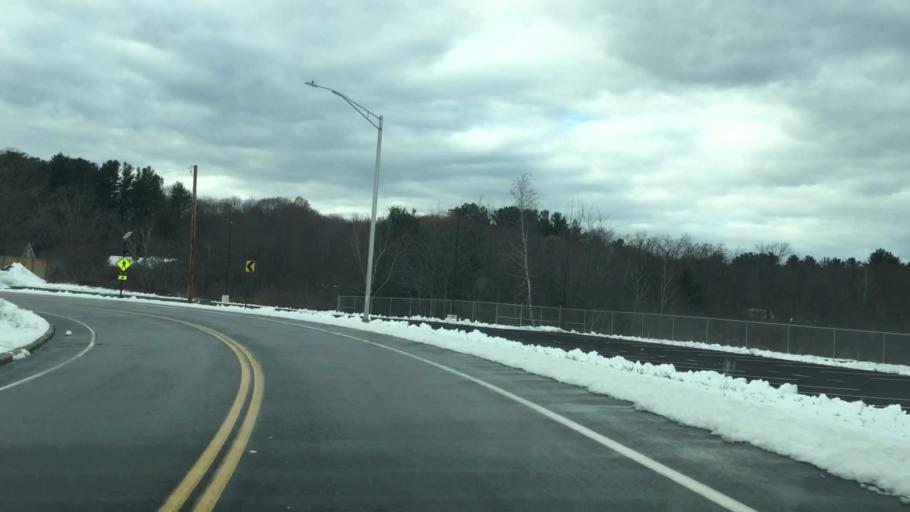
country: US
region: New Hampshire
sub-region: Rockingham County
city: Salem
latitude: 42.7733
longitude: -71.2311
